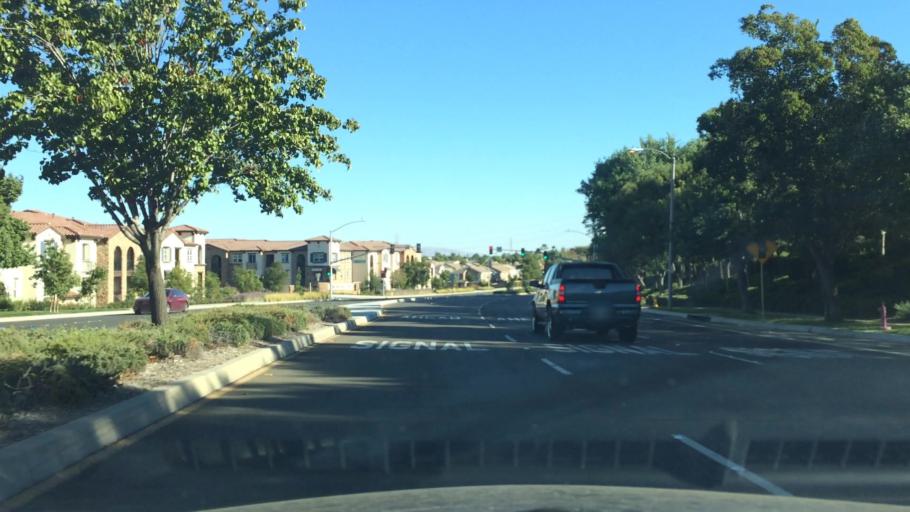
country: US
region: California
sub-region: San Bernardino County
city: Los Serranos
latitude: 33.9536
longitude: -117.6848
